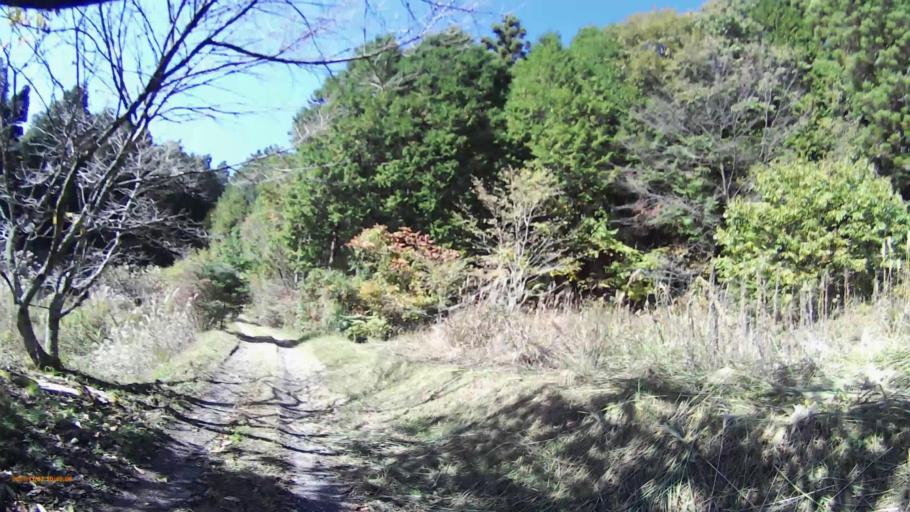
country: JP
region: Gifu
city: Mizunami
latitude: 35.4392
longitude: 137.3179
